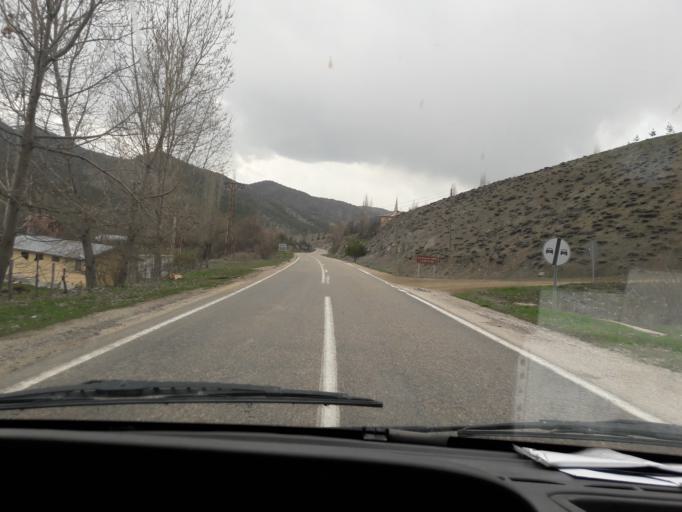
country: TR
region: Giresun
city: Alucra
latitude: 40.2752
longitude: 38.8416
